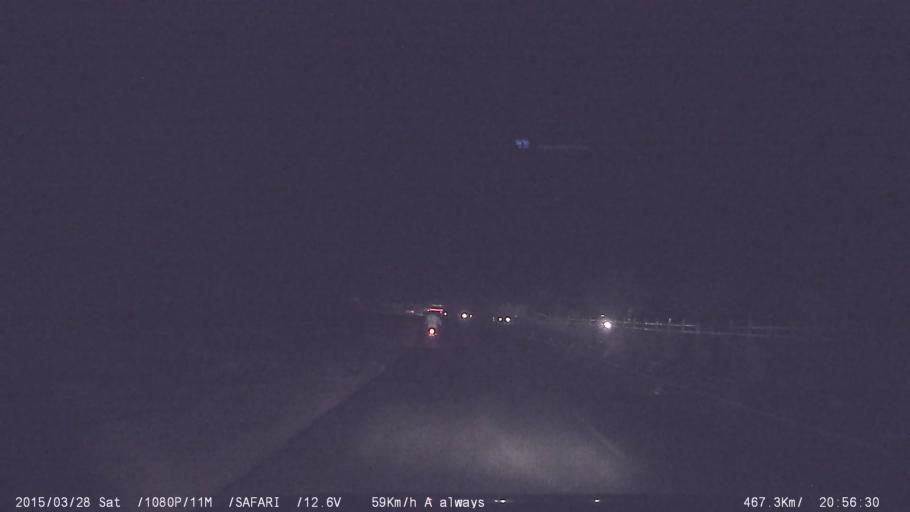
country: IN
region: Karnataka
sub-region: Ramanagara
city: Ramanagaram
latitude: 12.6917
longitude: 77.2432
